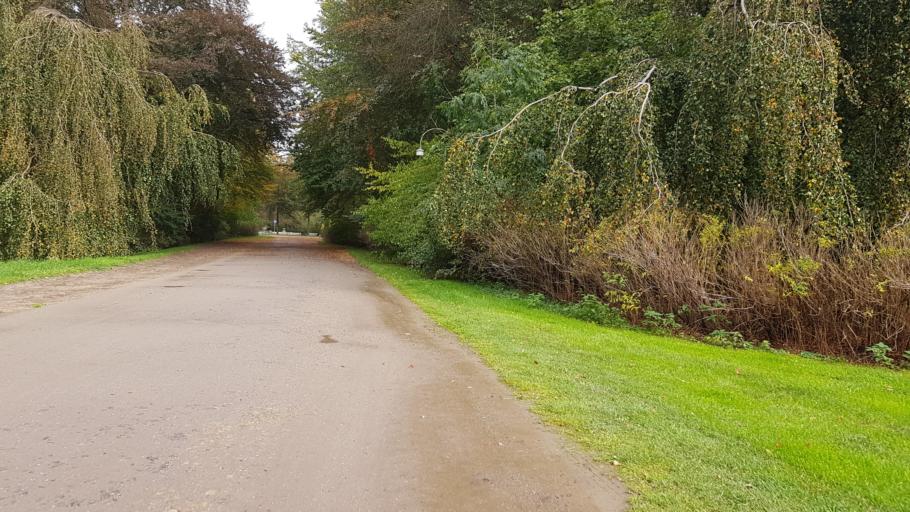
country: DE
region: Bremen
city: Bremen
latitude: 53.0901
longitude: 8.8175
